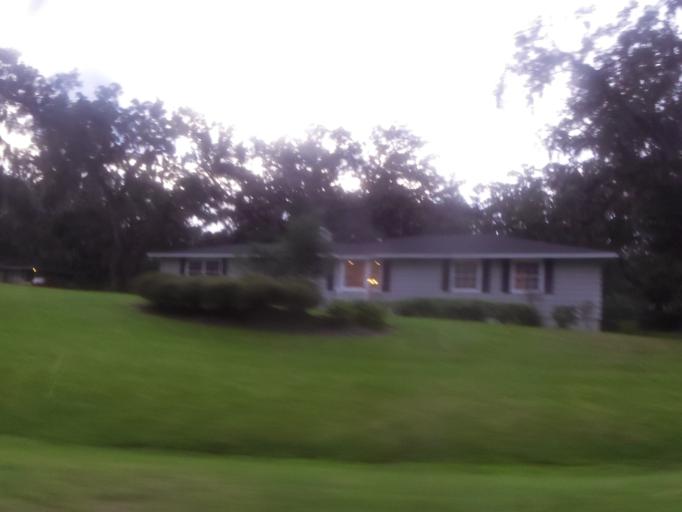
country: US
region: Florida
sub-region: Duval County
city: Jacksonville
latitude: 30.2689
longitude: -81.7029
